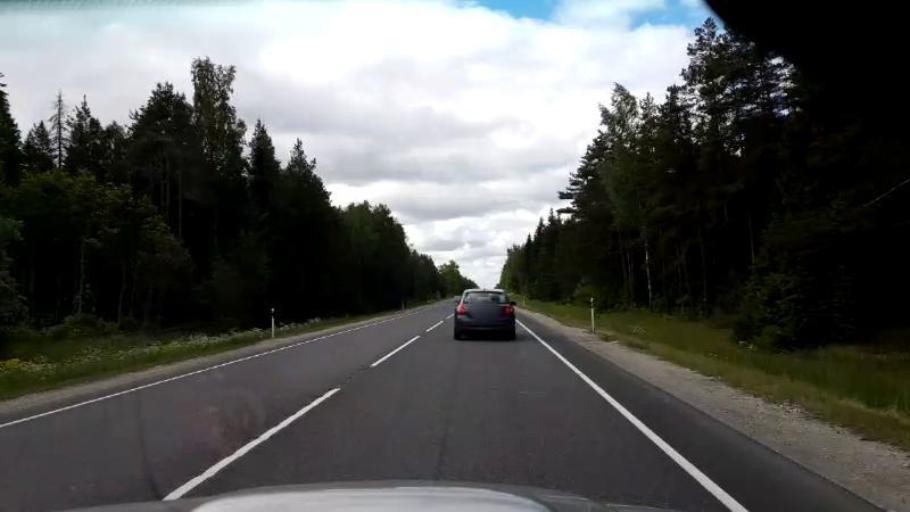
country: EE
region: Raplamaa
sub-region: Maerjamaa vald
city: Marjamaa
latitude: 58.8807
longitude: 24.4485
